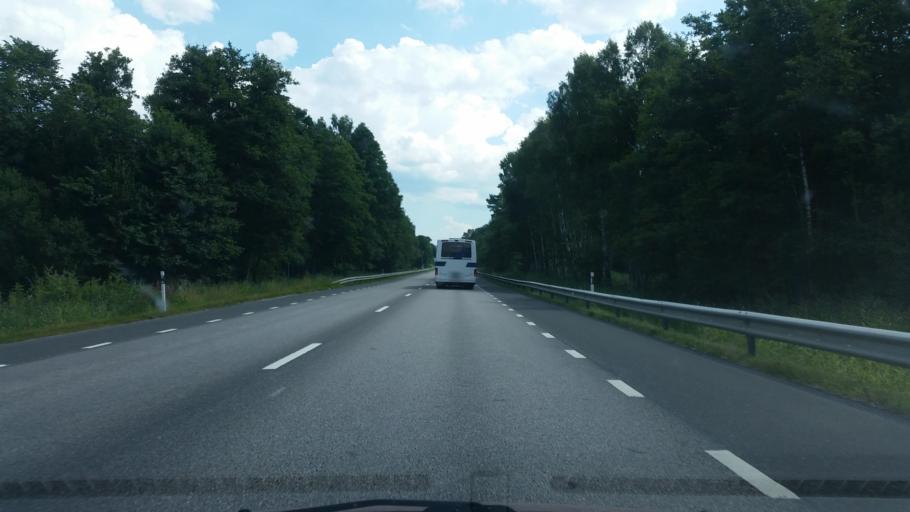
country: SE
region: Vaestra Goetaland
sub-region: Skara Kommun
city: Axvall
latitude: 58.3948
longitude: 13.6262
